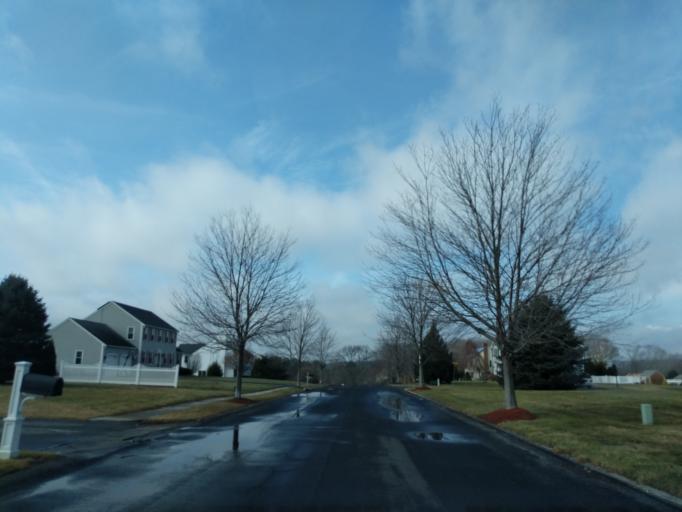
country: US
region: Massachusetts
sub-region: Worcester County
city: Whitinsville
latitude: 42.1038
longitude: -71.6778
